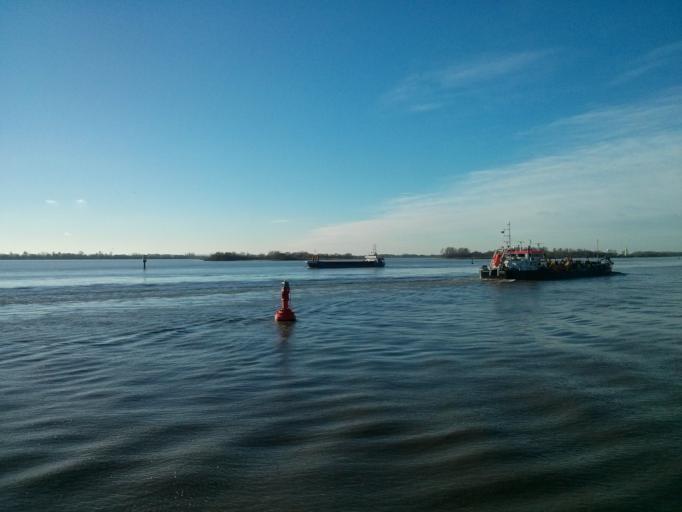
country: DE
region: Lower Saxony
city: Neu Wulmstorf
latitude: 53.5577
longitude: 9.7958
